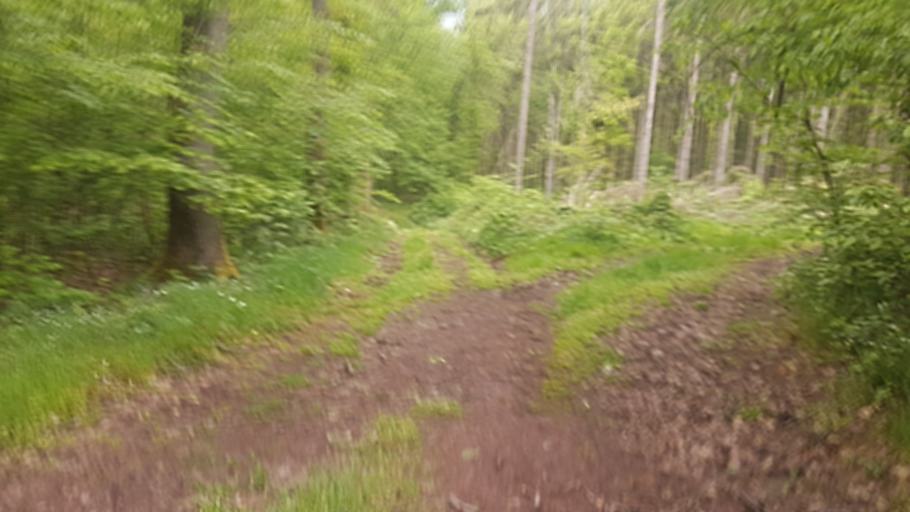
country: FR
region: Champagne-Ardenne
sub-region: Departement des Ardennes
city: Haybes
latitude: 50.0651
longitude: 4.6215
